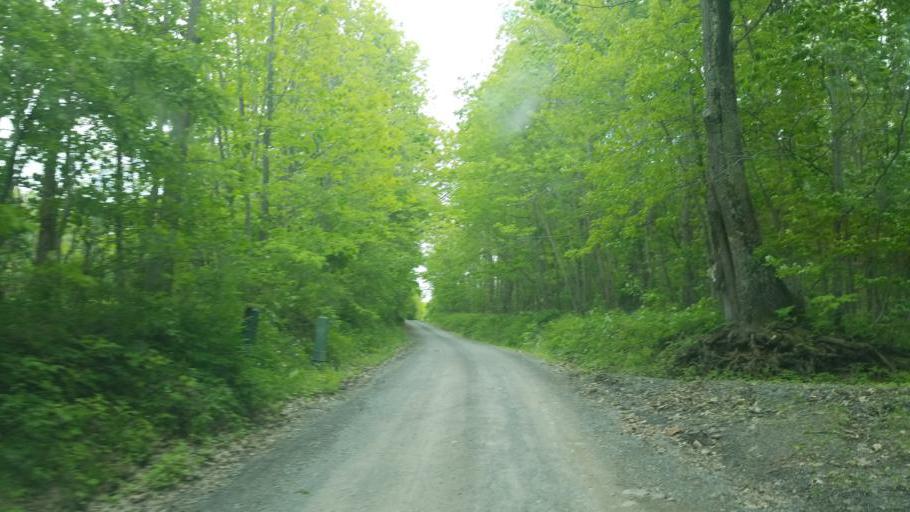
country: US
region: New York
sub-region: Otsego County
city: Richfield Springs
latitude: 42.8198
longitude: -74.9825
